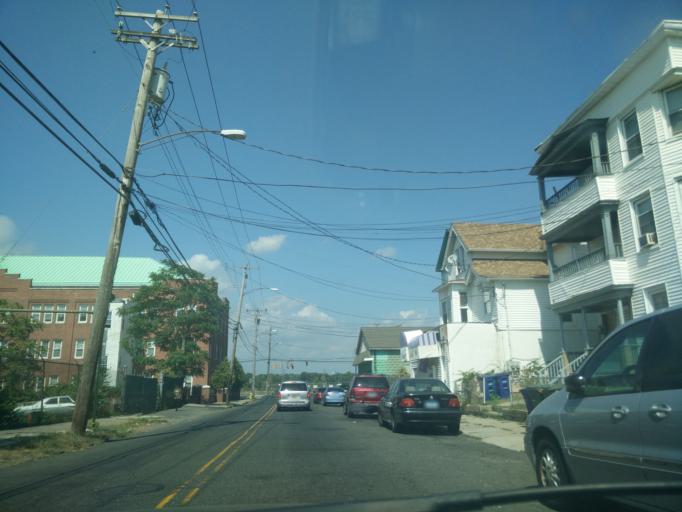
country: US
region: Connecticut
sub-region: Fairfield County
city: Stratford
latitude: 41.1924
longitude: -73.1702
